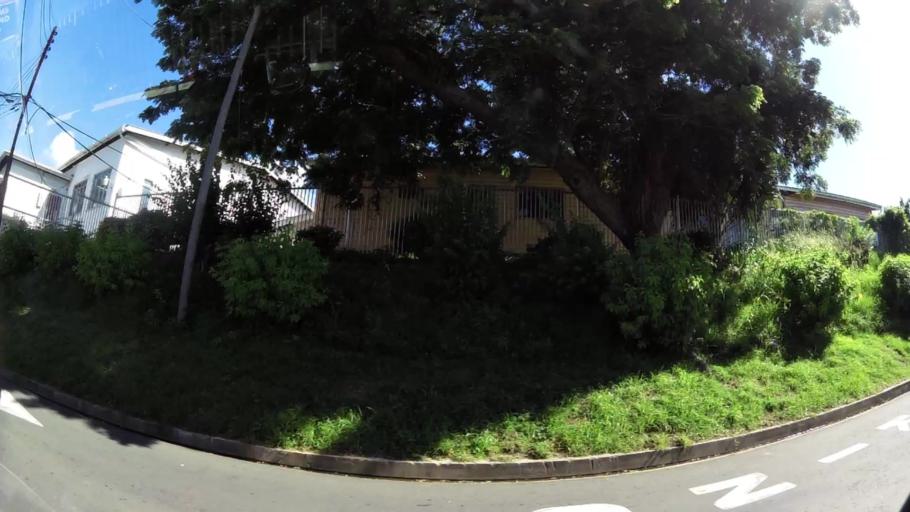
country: TT
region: Tobago
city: Scarborough
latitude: 11.1773
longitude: -60.7316
